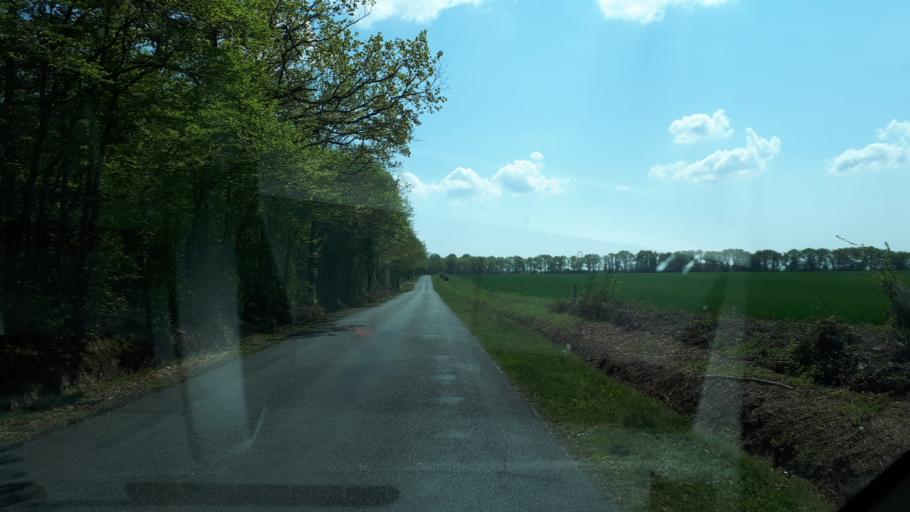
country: FR
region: Centre
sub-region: Departement du Cher
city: Neuvy-sur-Barangeon
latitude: 47.3223
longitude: 2.3372
